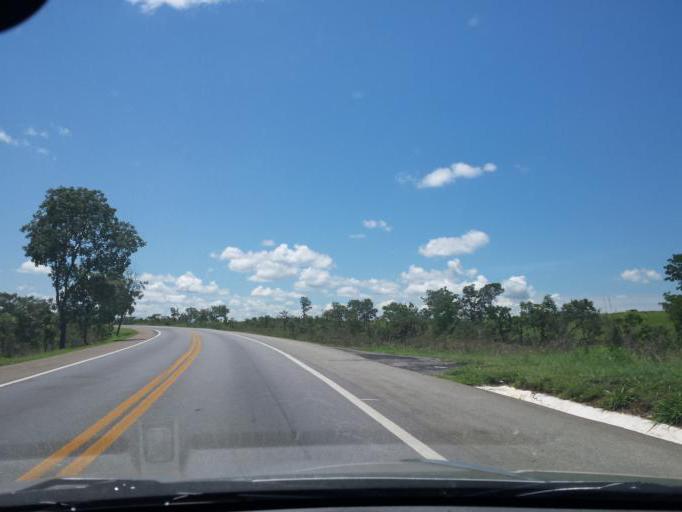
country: BR
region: Goias
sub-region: Luziania
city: Luziania
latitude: -16.4262
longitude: -47.8229
